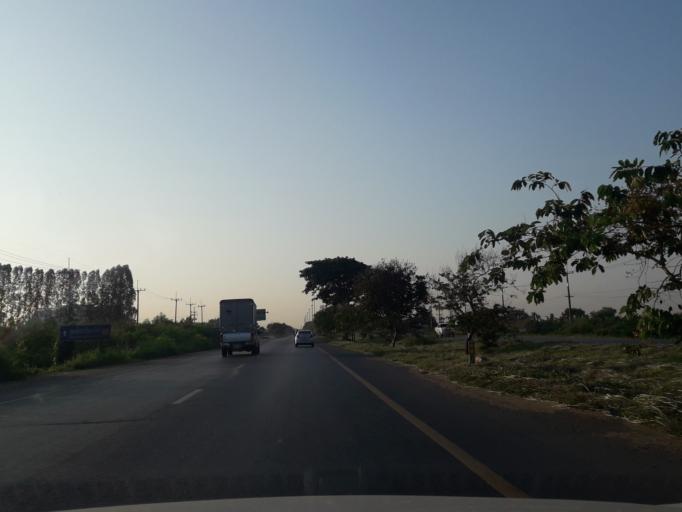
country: TH
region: Phra Nakhon Si Ayutthaya
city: Bang Pa-in
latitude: 14.2193
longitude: 100.5424
